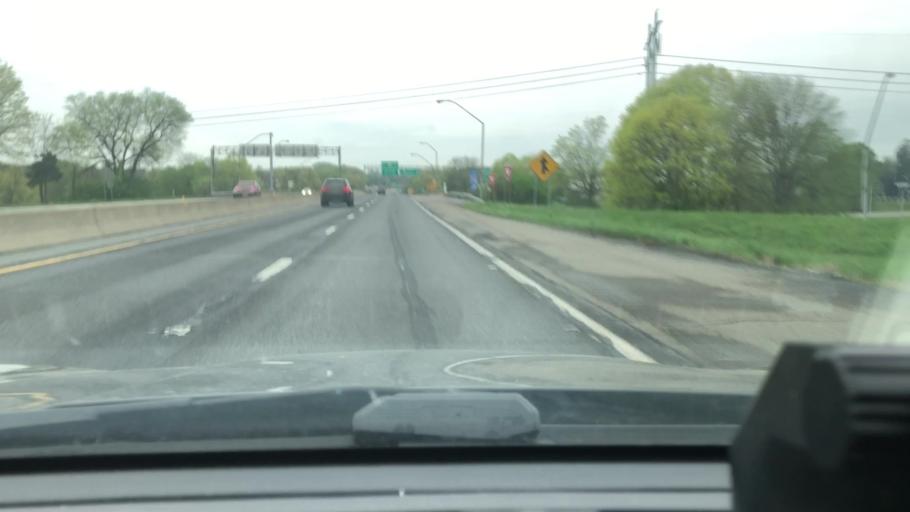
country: US
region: Pennsylvania
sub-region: Lehigh County
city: Wescosville
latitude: 40.6008
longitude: -75.5578
